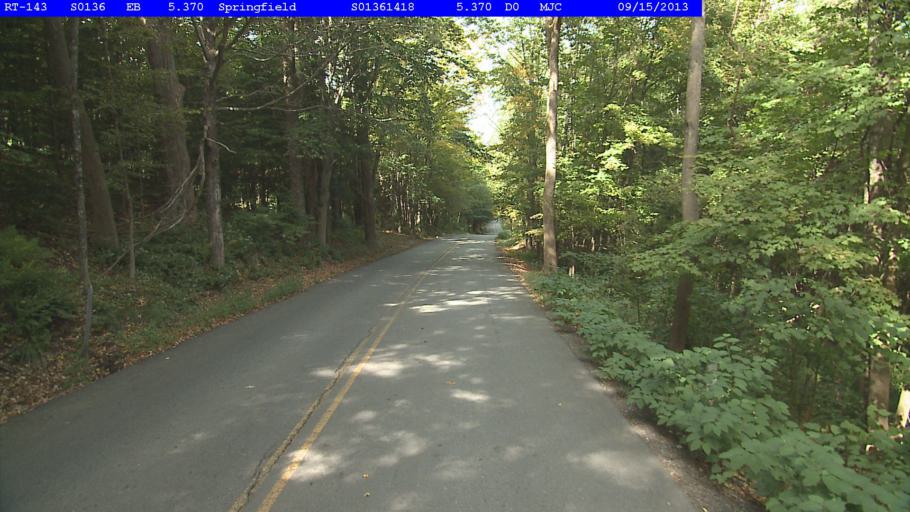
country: US
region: Vermont
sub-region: Windsor County
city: Springfield
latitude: 43.3260
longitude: -72.4123
